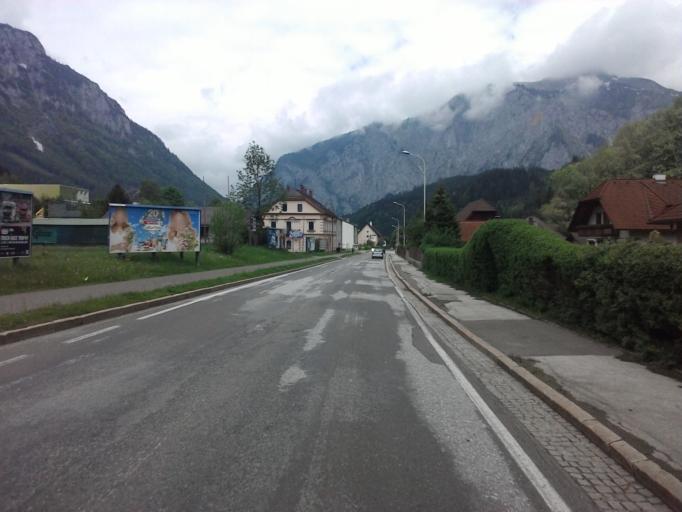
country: AT
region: Styria
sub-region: Politischer Bezirk Leoben
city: Eisenerz
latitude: 47.5526
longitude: 14.8736
